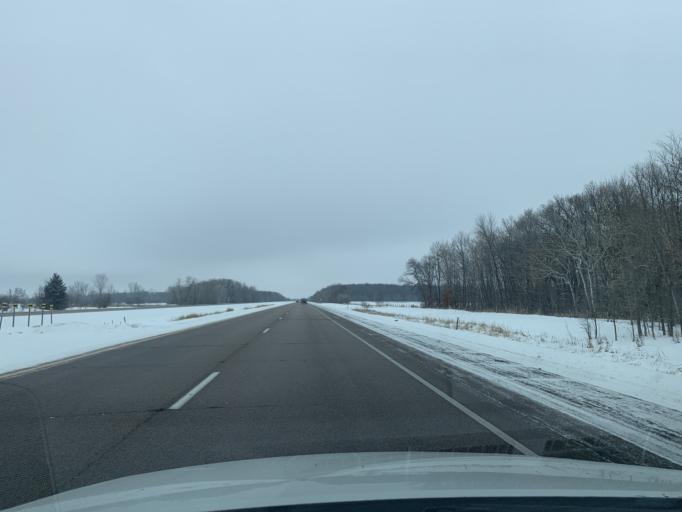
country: US
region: Minnesota
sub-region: Chisago County
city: Rush City
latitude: 45.6533
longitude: -92.9922
